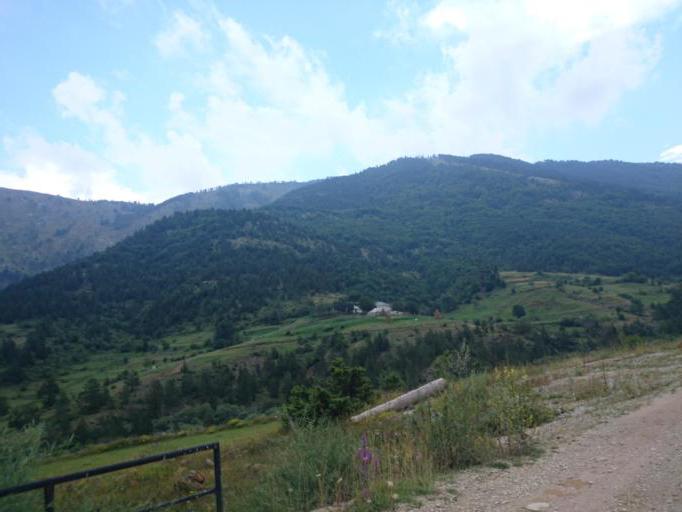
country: AL
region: Diber
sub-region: Rrethi i Dibres
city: Fushe-Lure
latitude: 41.7928
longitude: 20.2262
